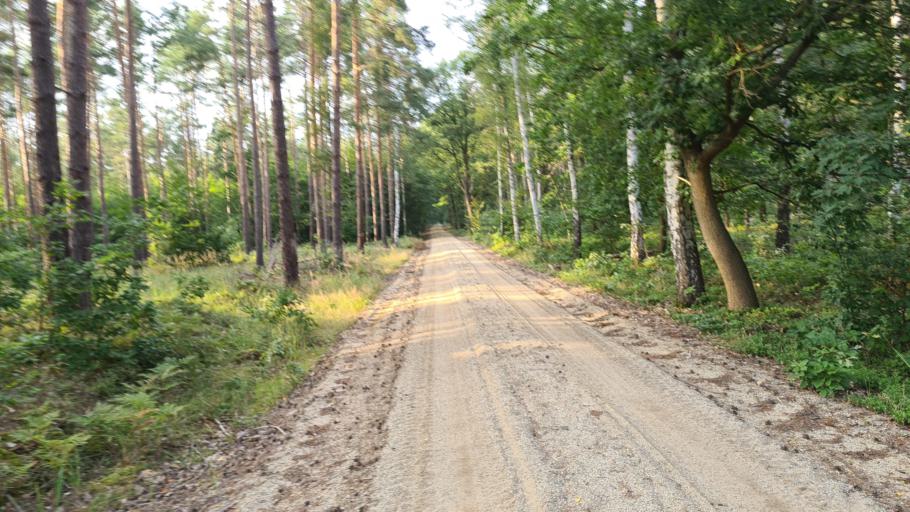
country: DE
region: Brandenburg
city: Trobitz
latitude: 51.6215
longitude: 13.4579
